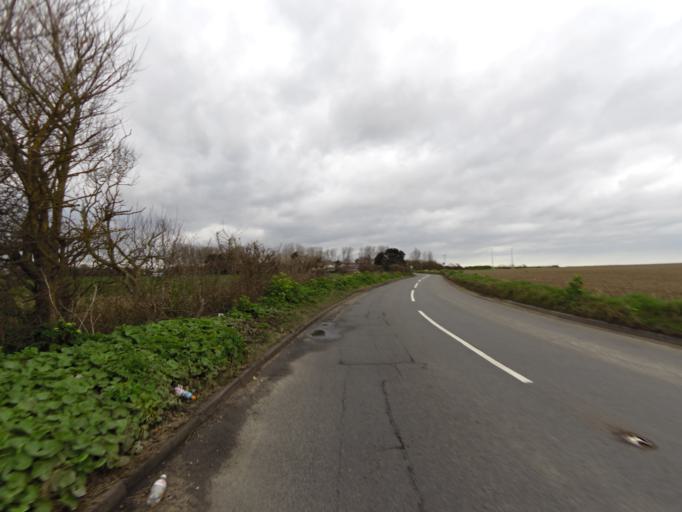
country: GB
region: England
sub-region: Norfolk
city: Hopton on Sea
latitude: 52.5191
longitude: 1.7428
